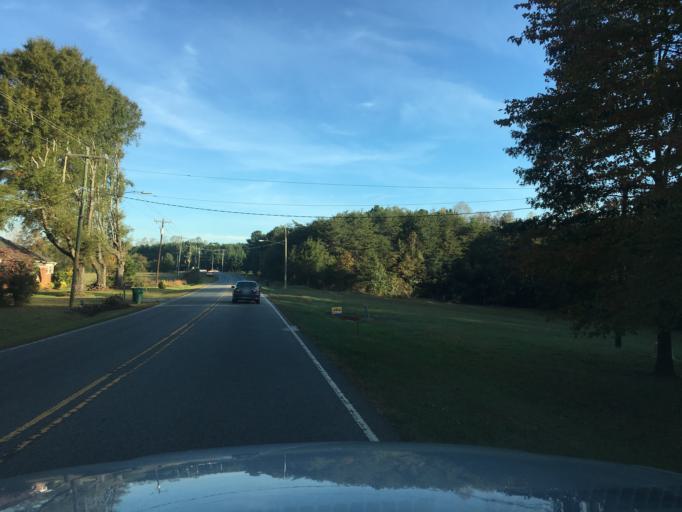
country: US
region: North Carolina
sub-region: Catawba County
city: Newton
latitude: 35.6544
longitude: -81.2663
